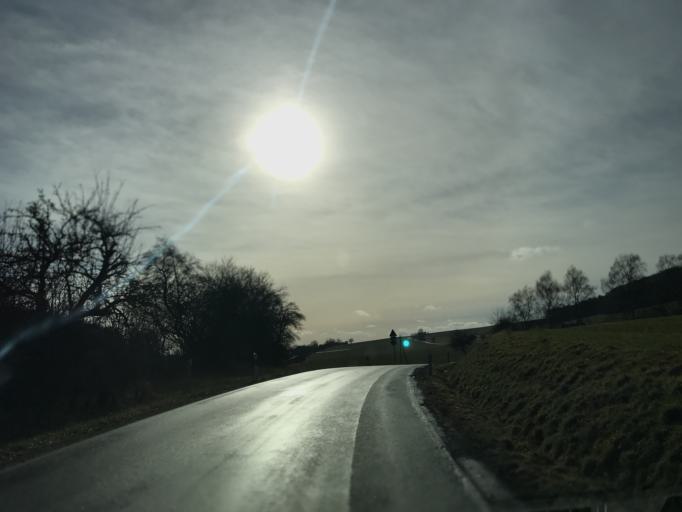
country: DE
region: Hesse
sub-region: Regierungsbezirk Kassel
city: Hofgeismar
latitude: 51.5247
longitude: 9.3864
